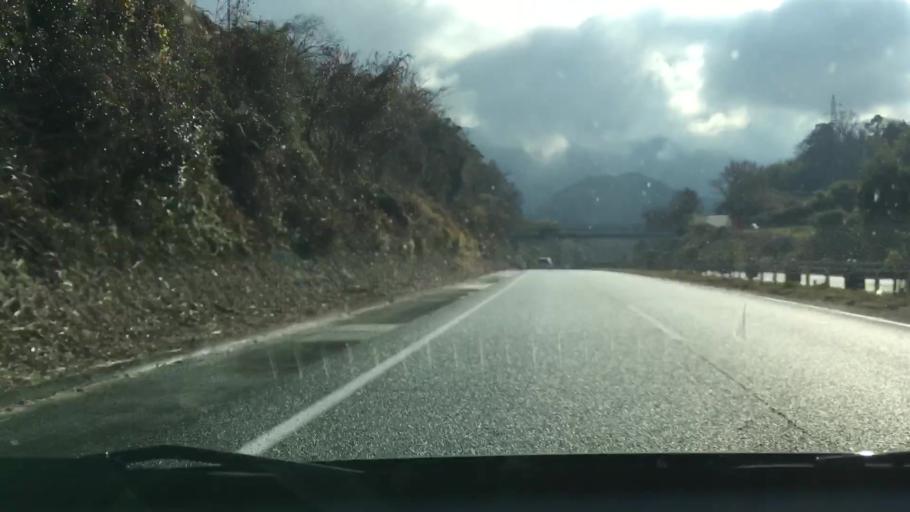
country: JP
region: Kumamoto
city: Matsubase
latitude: 32.5567
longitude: 130.6953
